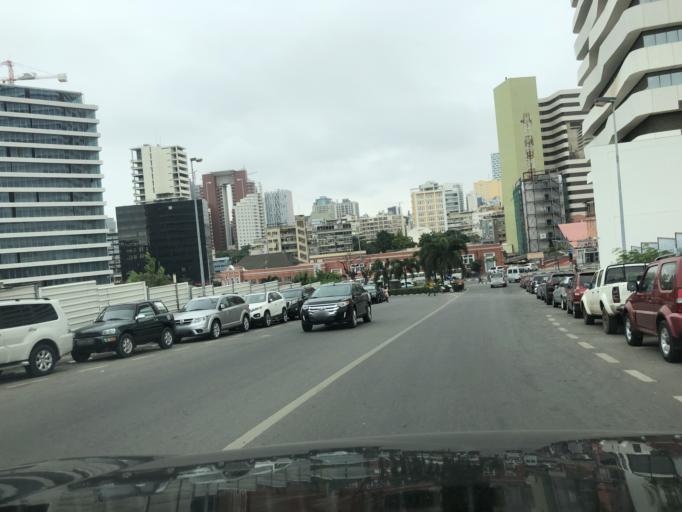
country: AO
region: Luanda
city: Luanda
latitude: -8.8165
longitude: 13.2288
